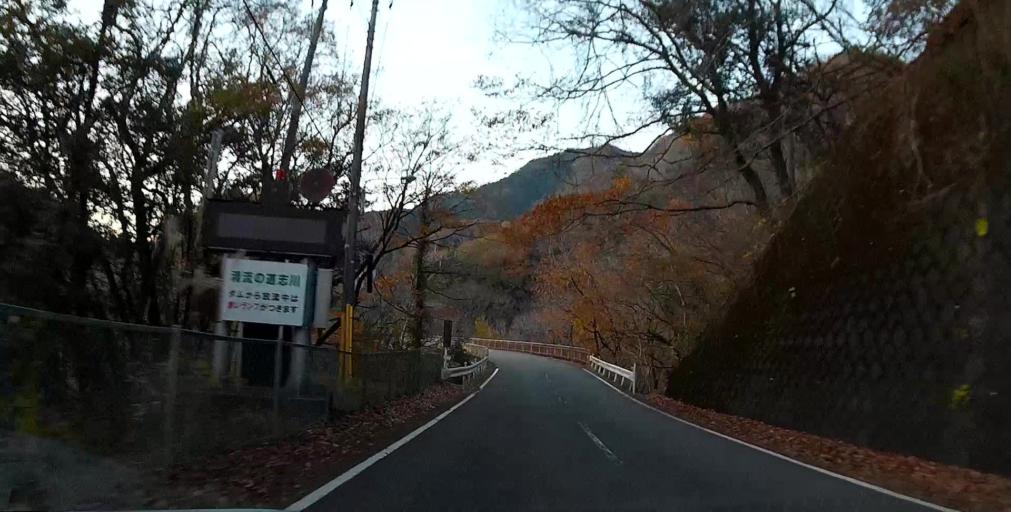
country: JP
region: Yamanashi
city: Uenohara
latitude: 35.5676
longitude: 139.2054
